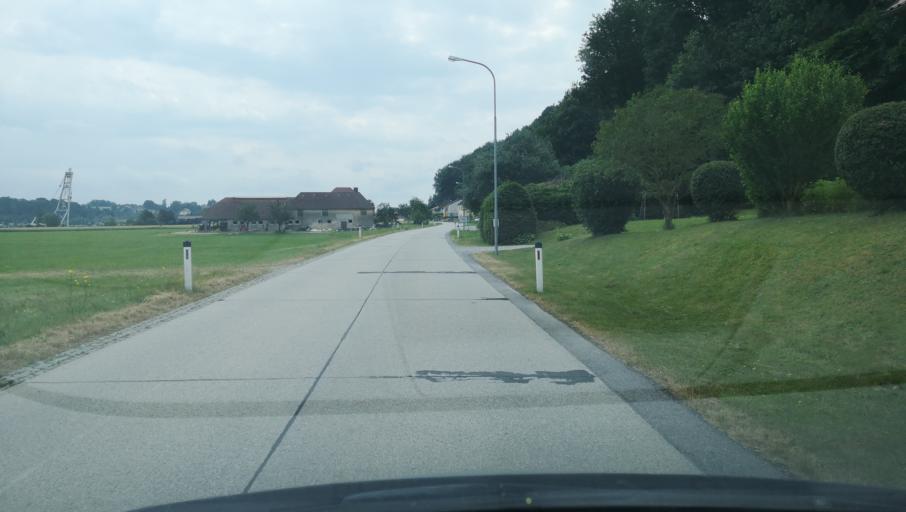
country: AT
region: Lower Austria
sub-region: Politischer Bezirk Melk
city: Ybbs an der Donau
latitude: 48.1934
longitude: 15.0538
